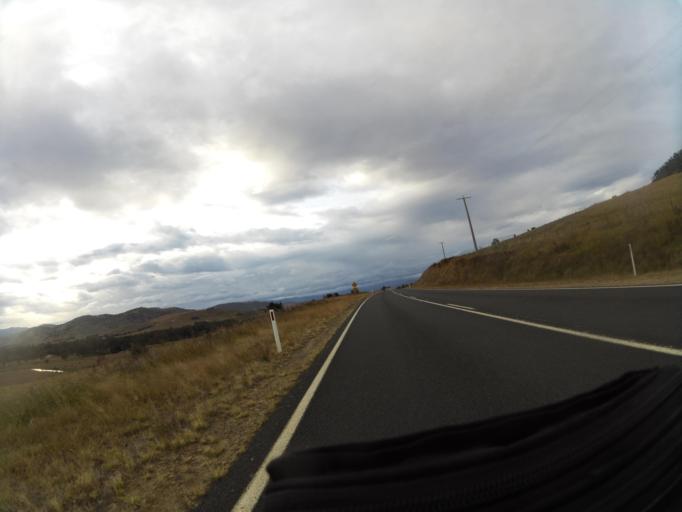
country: AU
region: New South Wales
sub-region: Snowy River
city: Jindabyne
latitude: -36.0806
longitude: 147.9751
